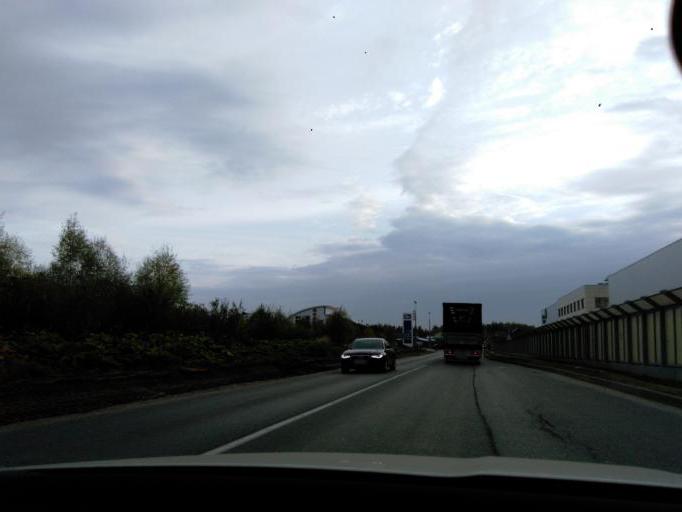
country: RU
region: Moskovskaya
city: Sheremet'yevskiy
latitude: 55.9701
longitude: 37.4473
